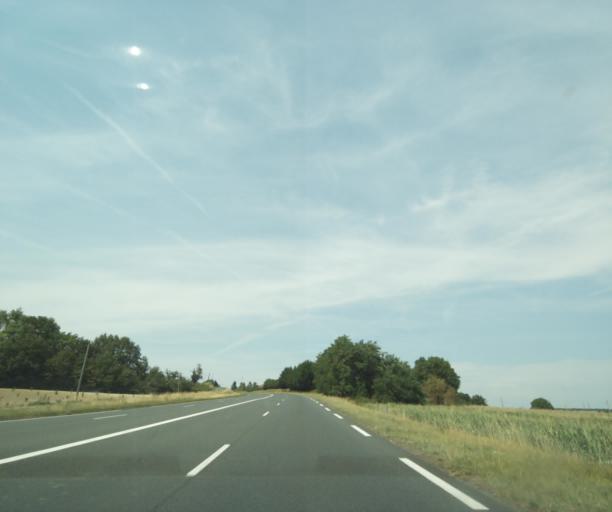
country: FR
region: Centre
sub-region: Departement d'Indre-et-Loire
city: La Celle-Saint-Avant
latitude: 47.0567
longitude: 0.6158
